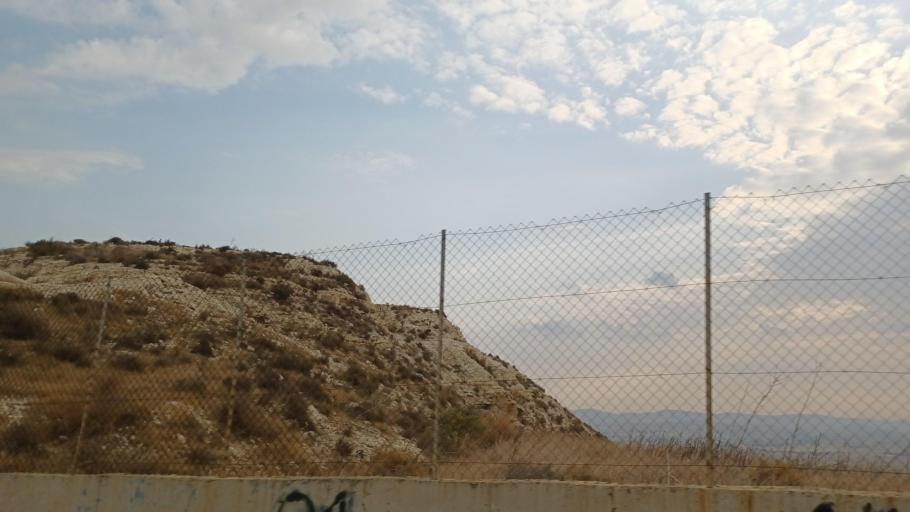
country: CY
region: Larnaka
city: Troulloi
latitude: 35.0288
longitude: 33.5749
